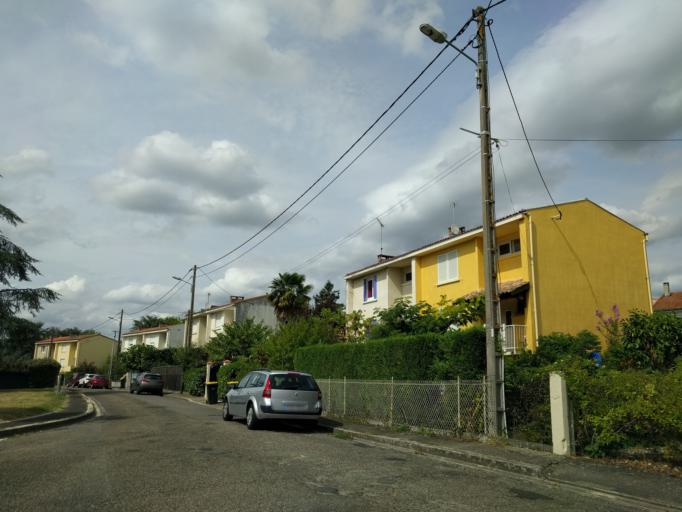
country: FR
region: Aquitaine
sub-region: Departement du Lot-et-Garonne
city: Agen
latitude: 44.1909
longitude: 0.6316
